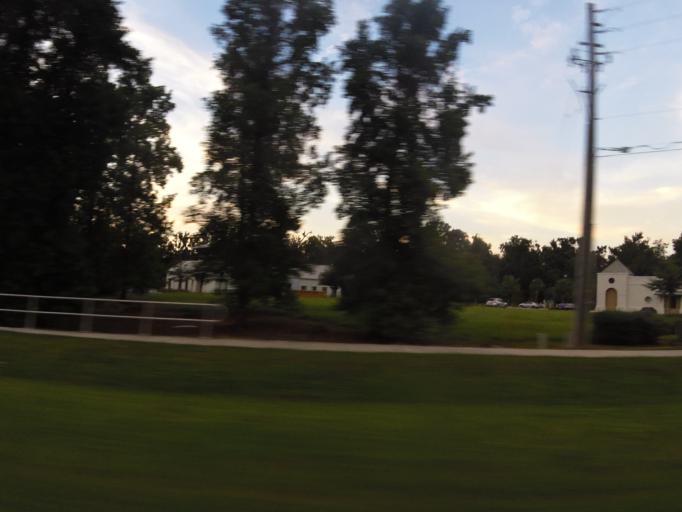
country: US
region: Florida
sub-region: Saint Johns County
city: Fruit Cove
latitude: 30.1095
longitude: -81.5660
